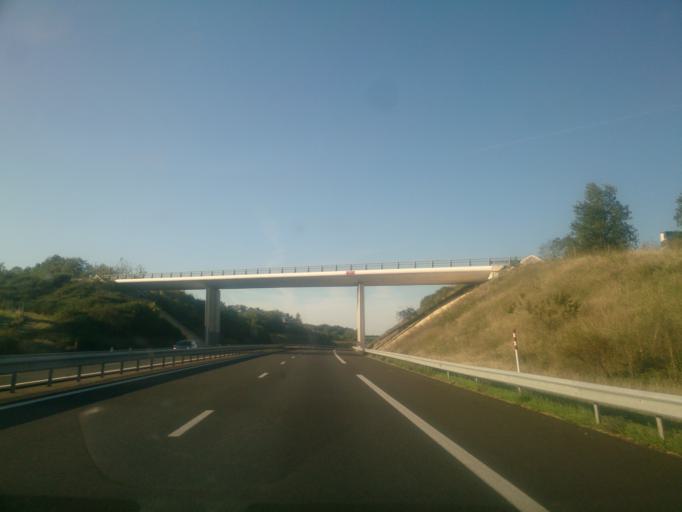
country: FR
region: Midi-Pyrenees
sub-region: Departement du Lot
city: Le Vigan
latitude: 44.6107
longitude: 1.5004
